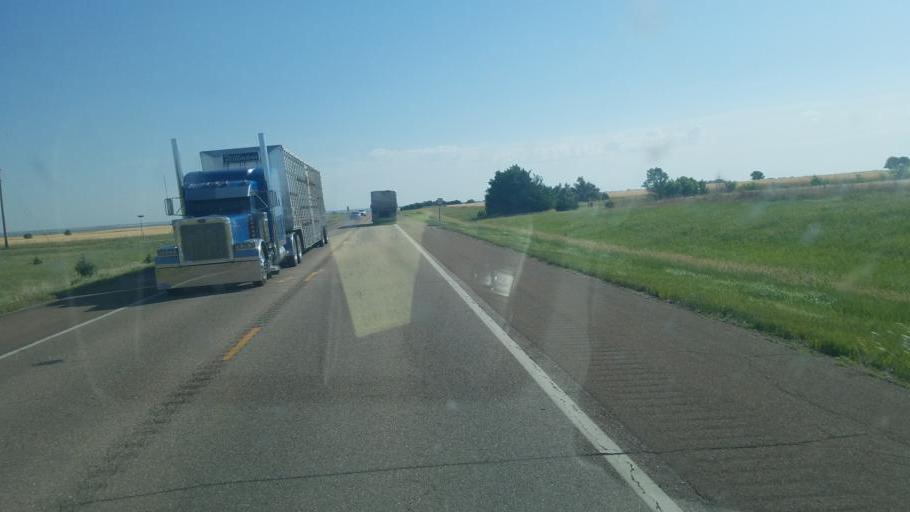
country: US
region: Kansas
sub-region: Barton County
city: Ellinwood
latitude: 38.4067
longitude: -98.6642
